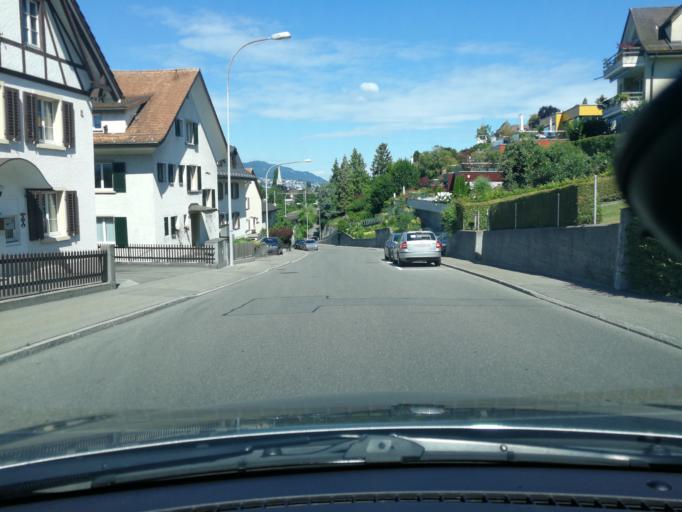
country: CH
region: Zurich
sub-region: Bezirk Meilen
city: Erlenbach / links des Dorfbachs oberhalb Bahnlinie
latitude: 47.2986
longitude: 8.5986
